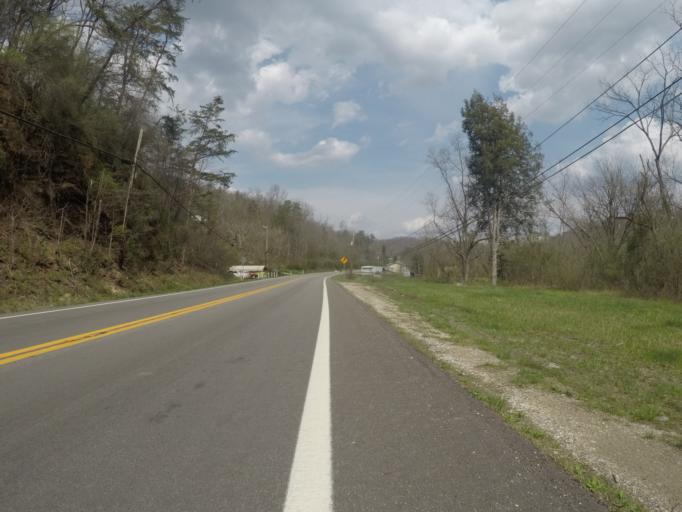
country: US
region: West Virginia
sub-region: Cabell County
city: Pea Ridge
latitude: 38.3885
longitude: -82.3307
